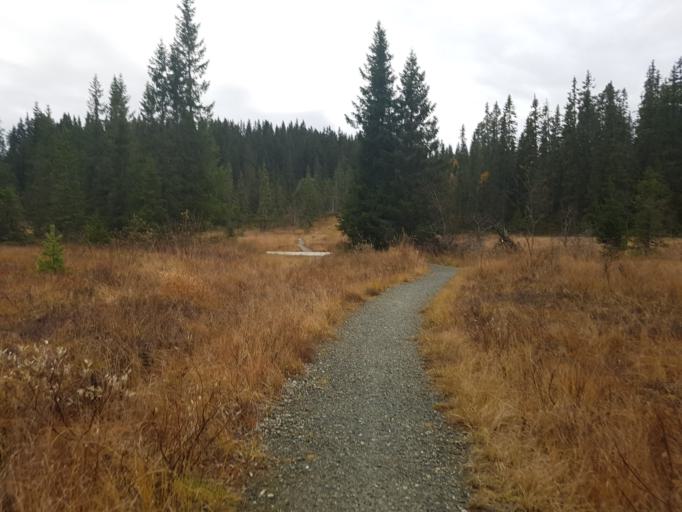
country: NO
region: Sor-Trondelag
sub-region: Melhus
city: Melhus
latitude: 63.3879
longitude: 10.2430
